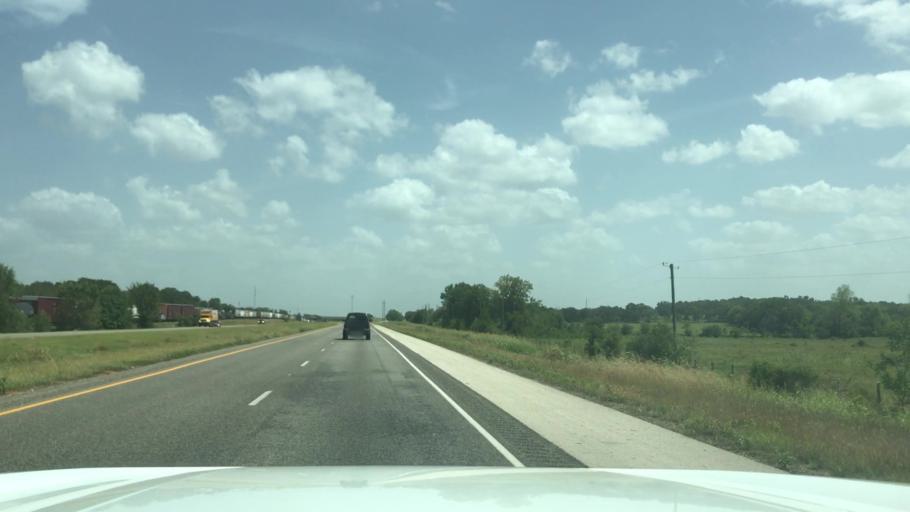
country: US
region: Texas
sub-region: Robertson County
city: Hearne
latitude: 30.9142
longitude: -96.6169
